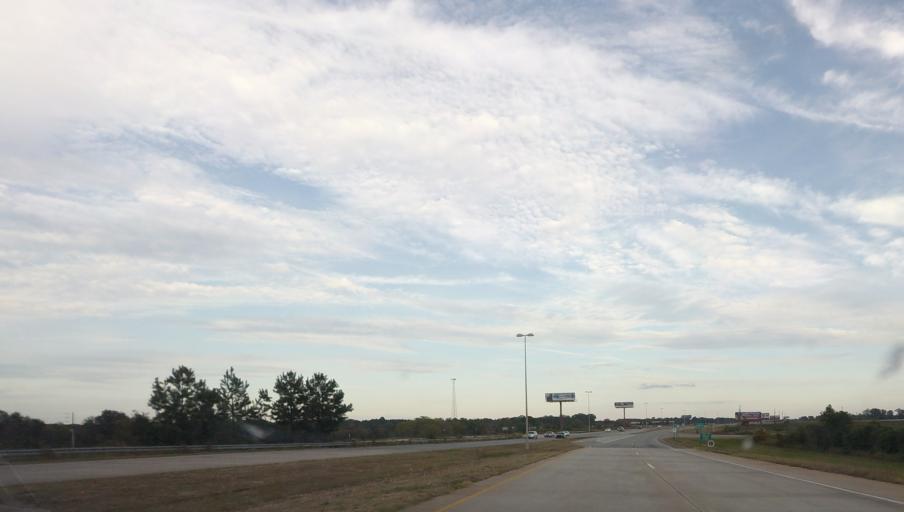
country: US
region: Georgia
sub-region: Houston County
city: Centerville
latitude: 32.5865
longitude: -83.7406
